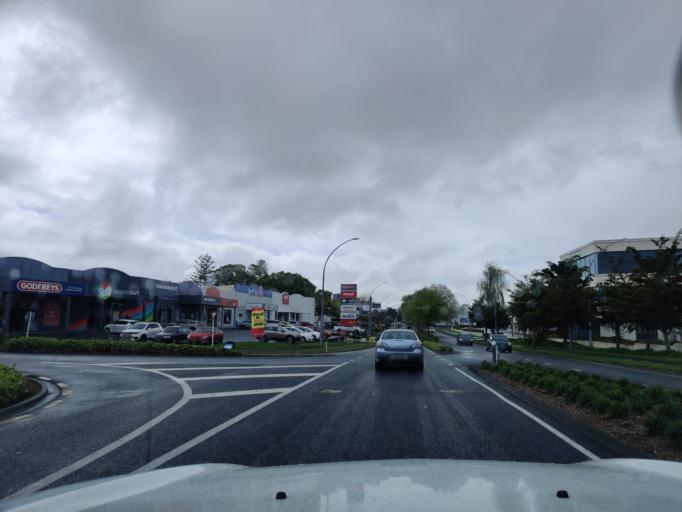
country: NZ
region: Waikato
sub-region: Hamilton City
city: Hamilton
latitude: -37.7942
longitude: 175.2834
